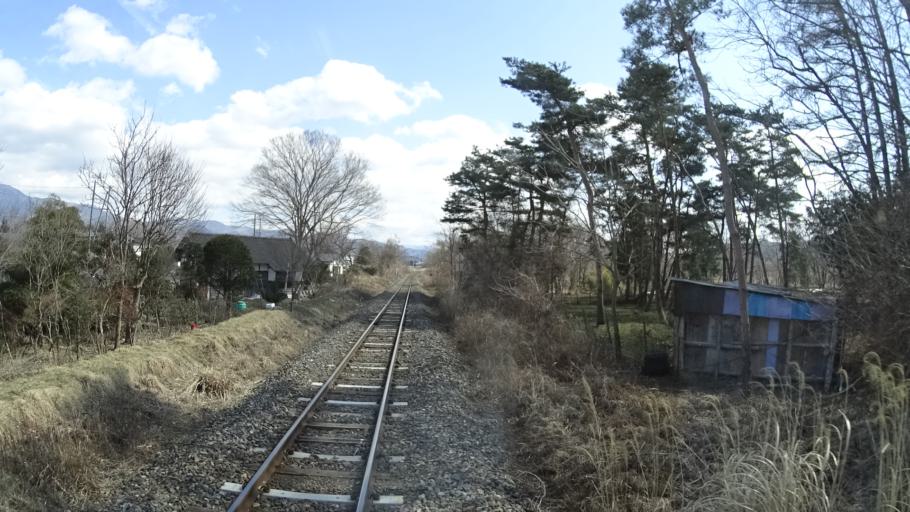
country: JP
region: Iwate
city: Tono
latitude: 39.3207
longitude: 141.5603
